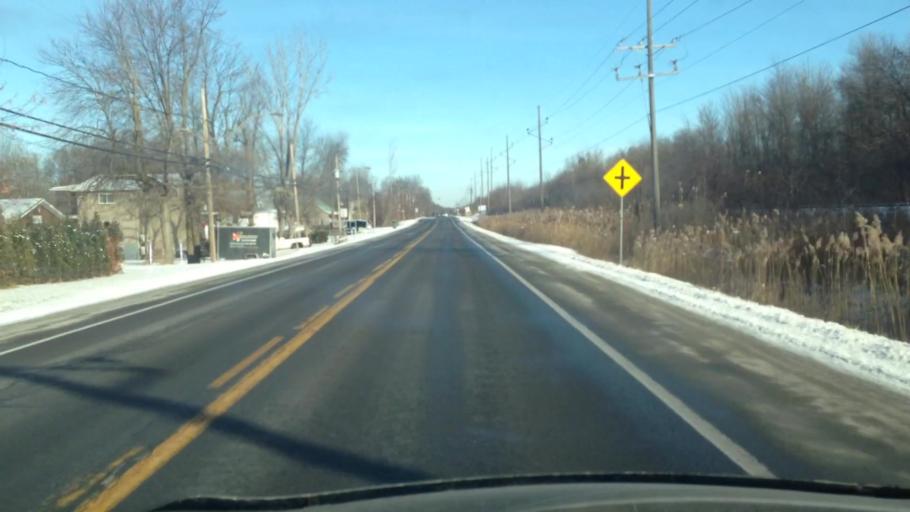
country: CA
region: Quebec
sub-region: Monteregie
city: Beauharnois
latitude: 45.3328
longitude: -73.8185
